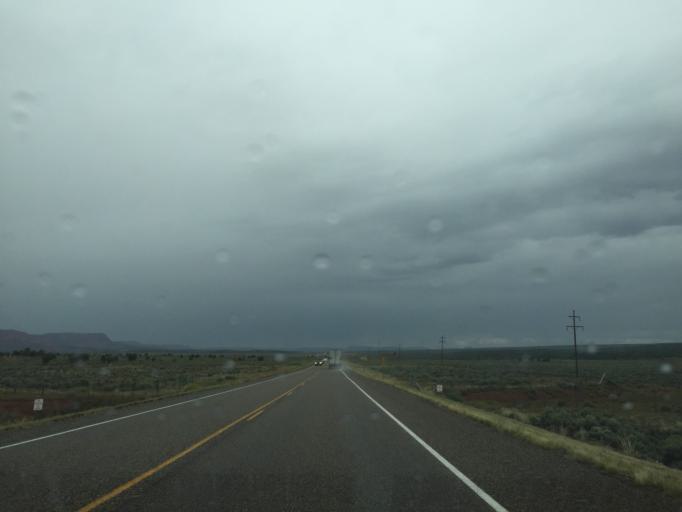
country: US
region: Utah
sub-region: Kane County
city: Kanab
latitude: 37.1074
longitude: -112.1224
